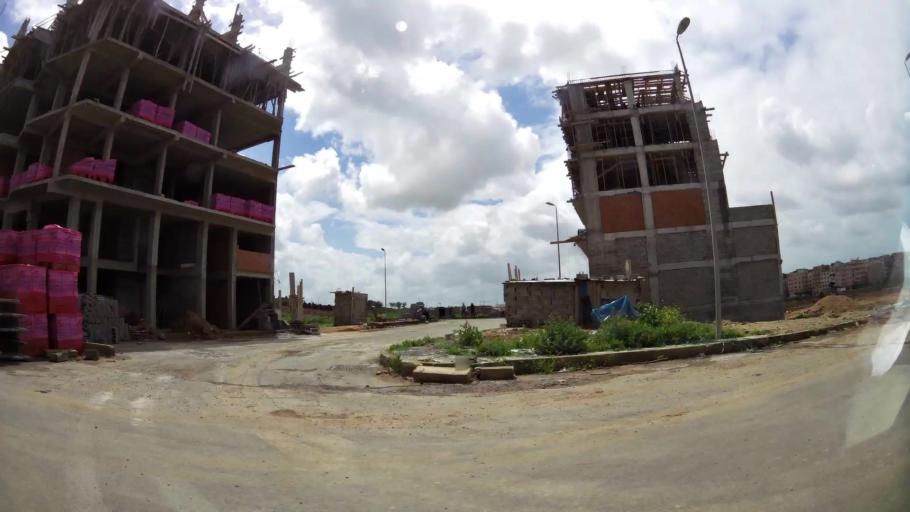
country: MA
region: Grand Casablanca
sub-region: Casablanca
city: Casablanca
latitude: 33.5284
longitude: -7.6034
